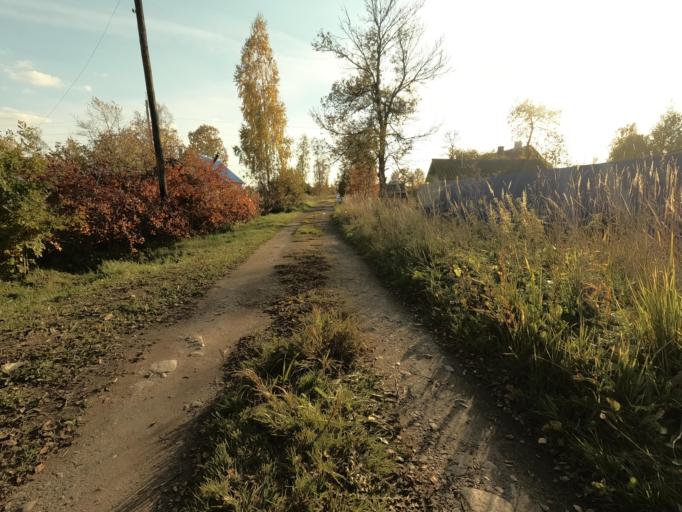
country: RU
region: Leningrad
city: Mga
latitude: 59.7511
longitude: 31.0624
